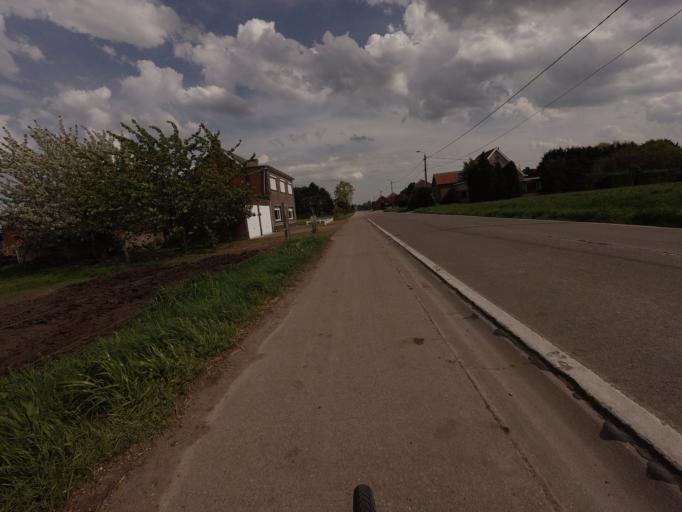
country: BE
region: Flanders
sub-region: Provincie Antwerpen
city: Putte
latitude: 51.0685
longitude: 4.6193
